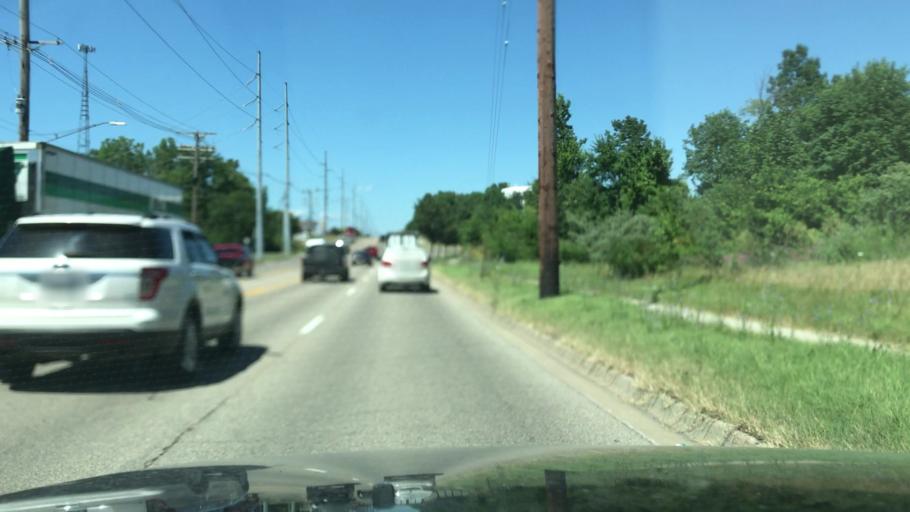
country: US
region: Michigan
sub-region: Ottawa County
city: Holland
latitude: 42.7772
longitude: -86.0774
